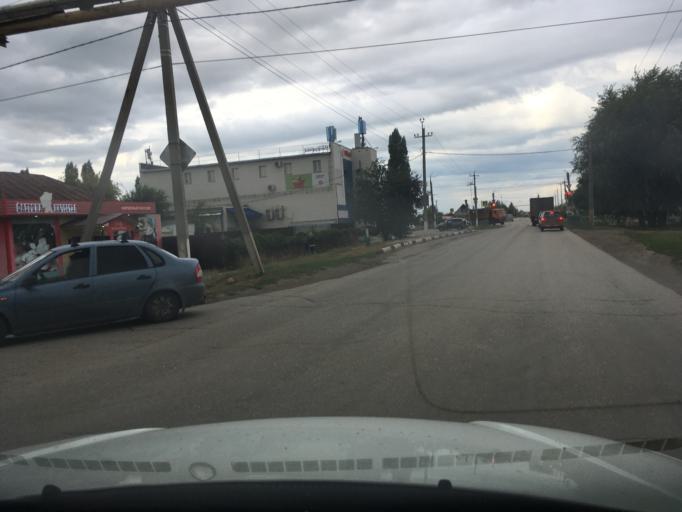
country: RU
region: Samara
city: Bezenchuk
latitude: 52.9833
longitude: 49.4329
